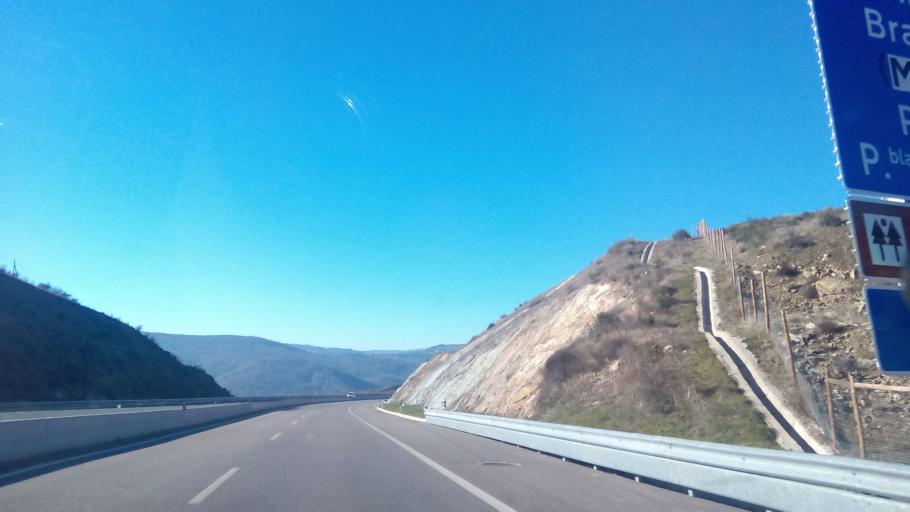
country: PT
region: Braganca
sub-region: Braganca Municipality
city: Braganca
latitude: 41.7814
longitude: -6.6978
